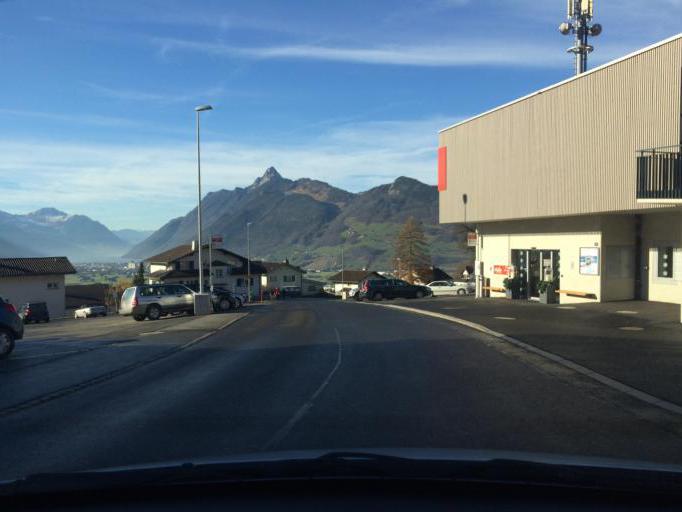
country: CH
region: Schwyz
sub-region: Bezirk Schwyz
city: Schwyz
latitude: 47.0146
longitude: 8.6696
